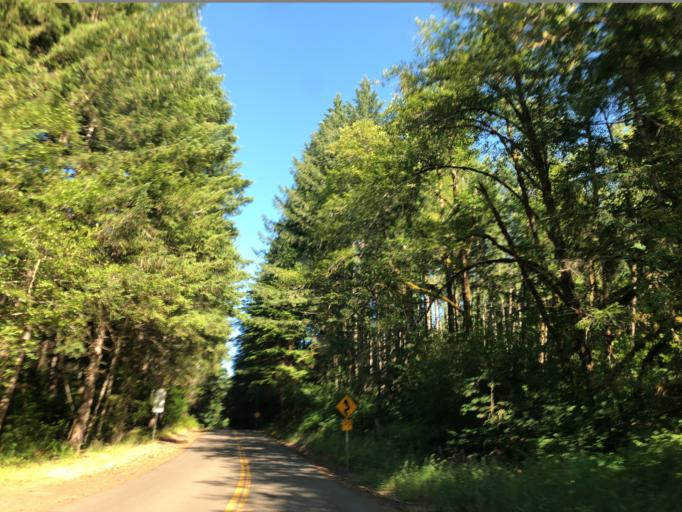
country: US
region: Oregon
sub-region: Linn County
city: Sweet Home
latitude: 44.4652
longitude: -122.6753
